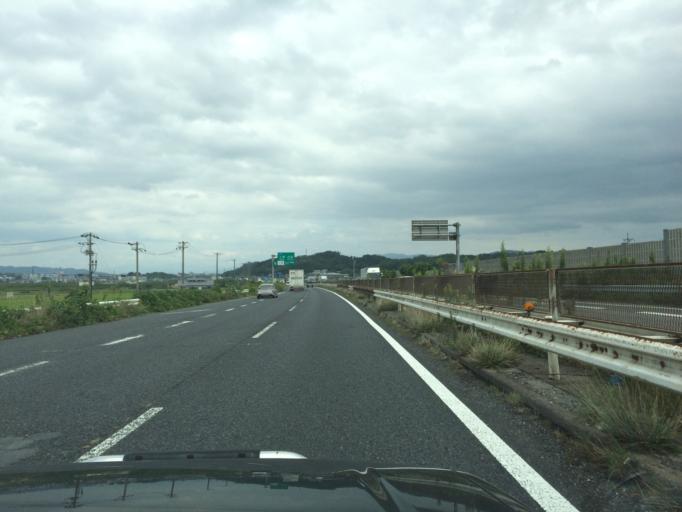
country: JP
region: Mie
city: Ueno-ebisumachi
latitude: 34.7401
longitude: 136.1129
